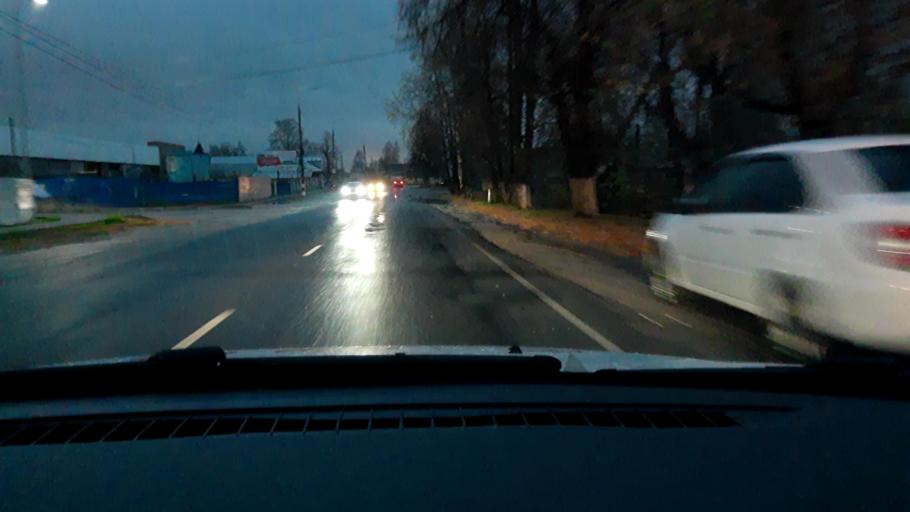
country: RU
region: Nizjnij Novgorod
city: Bor
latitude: 56.3706
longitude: 44.0358
